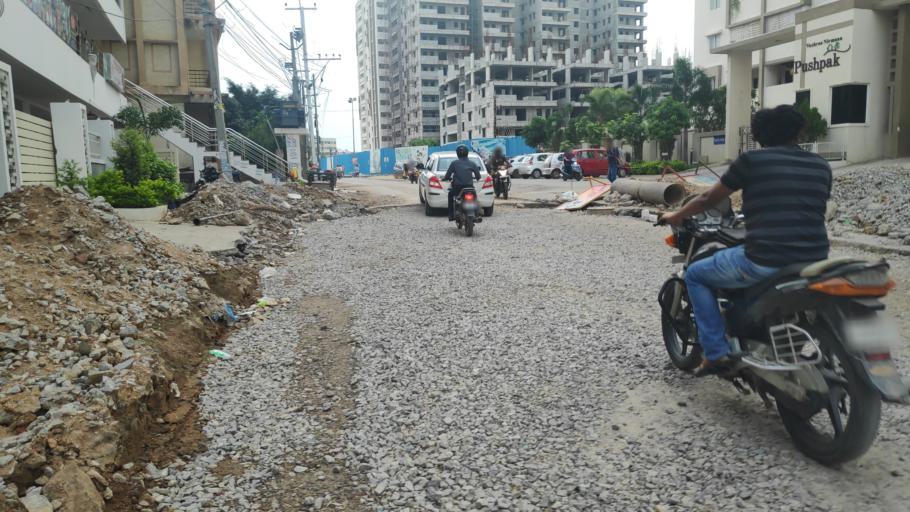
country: IN
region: Telangana
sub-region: Rangareddi
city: Kukatpalli
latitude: 17.5137
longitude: 78.3867
